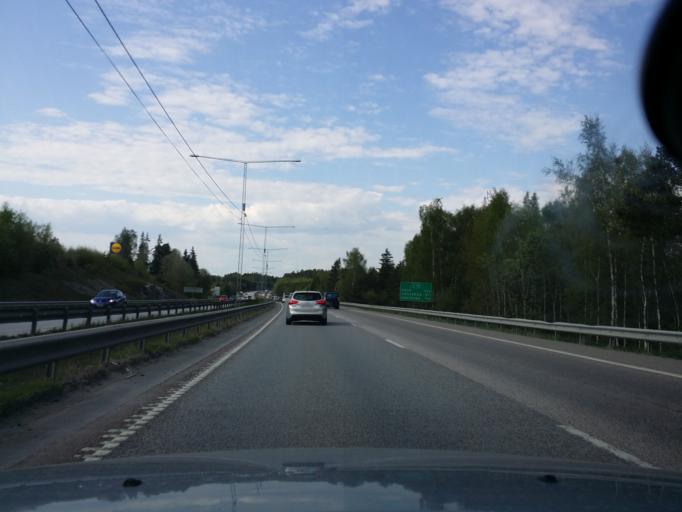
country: SE
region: Stockholm
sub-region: Jarfalla Kommun
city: Jakobsberg
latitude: 59.4281
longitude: 17.8497
